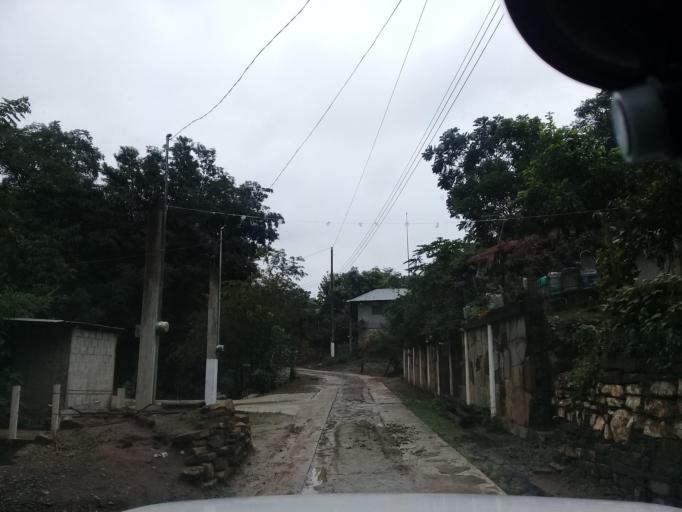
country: MX
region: Veracruz
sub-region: Chalma
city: San Pedro Coyutla
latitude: 21.2436
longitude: -98.4242
